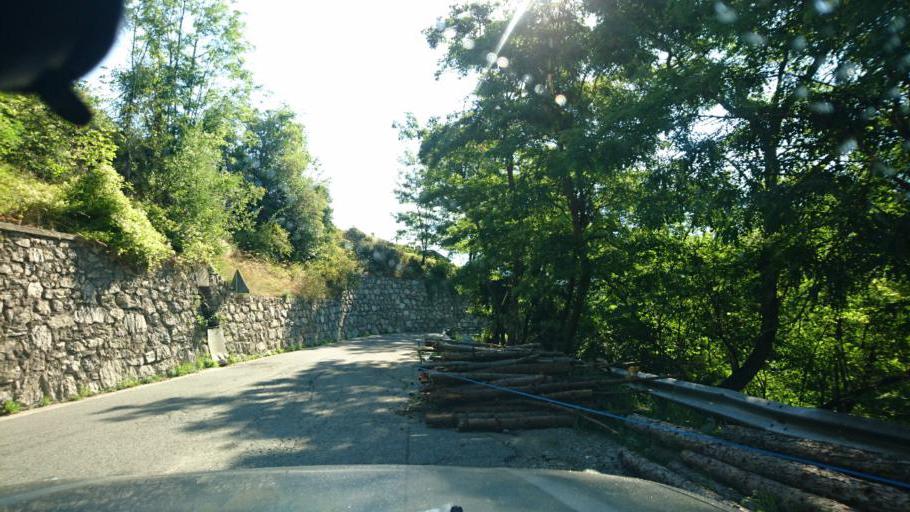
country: IT
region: Aosta Valley
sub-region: Valle d'Aosta
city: Villeneuve
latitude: 45.7236
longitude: 7.2001
